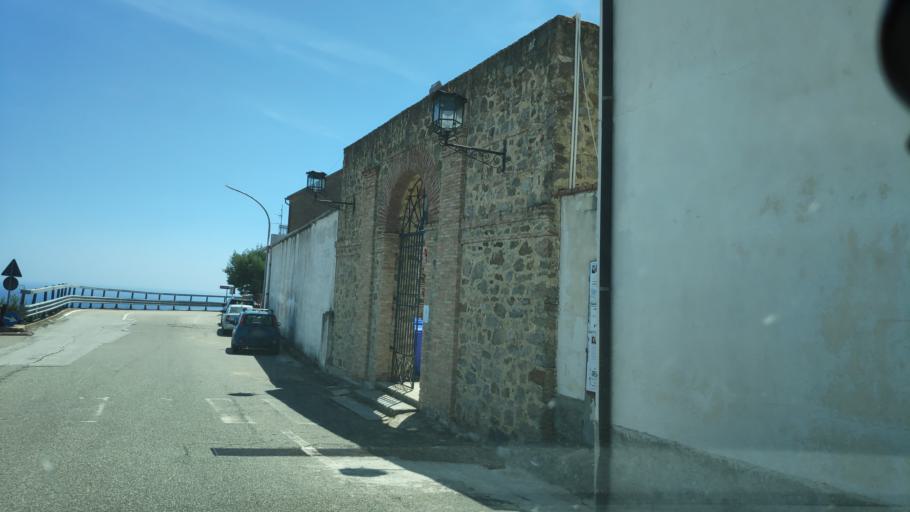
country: IT
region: Calabria
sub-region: Provincia di Catanzaro
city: Gasperina
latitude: 38.7364
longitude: 16.5131
